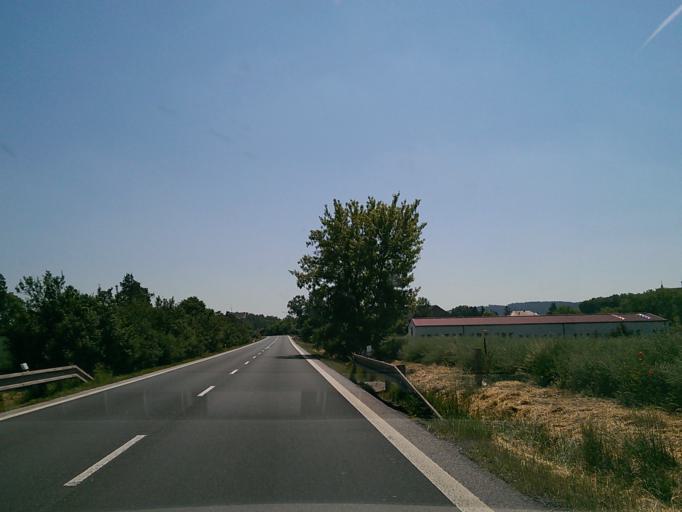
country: CZ
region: Liberecky
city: Rovensko pod Troskami
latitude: 50.5117
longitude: 15.2587
